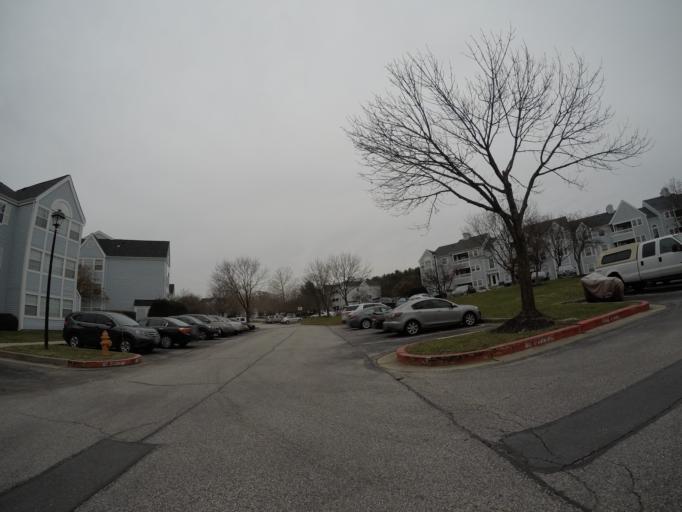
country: US
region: Maryland
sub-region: Howard County
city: Columbia
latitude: 39.2195
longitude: -76.7984
